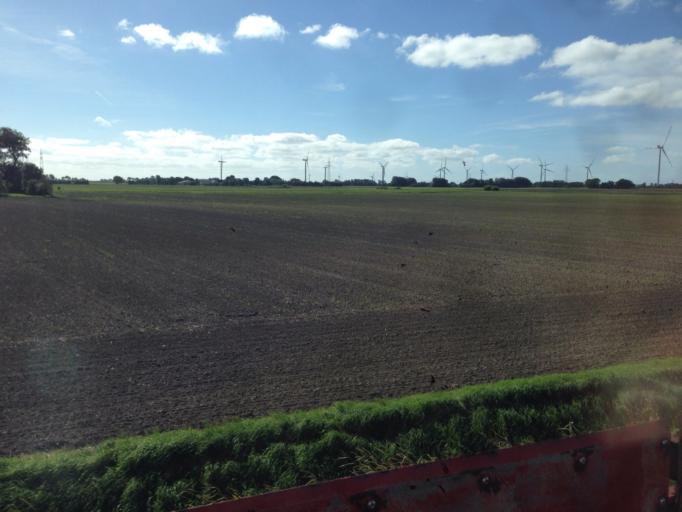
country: DE
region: Schleswig-Holstein
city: Niebull
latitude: 54.8119
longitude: 8.7843
